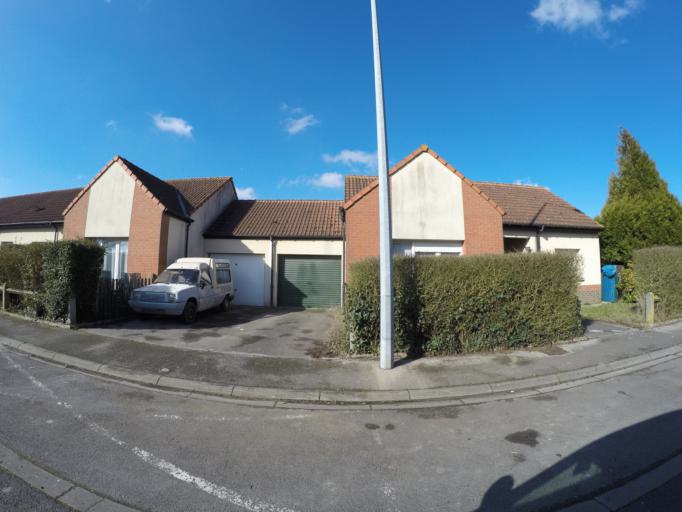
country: FR
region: Nord-Pas-de-Calais
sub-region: Departement du Pas-de-Calais
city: Bully-les-Mines
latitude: 50.4572
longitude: 2.7220
